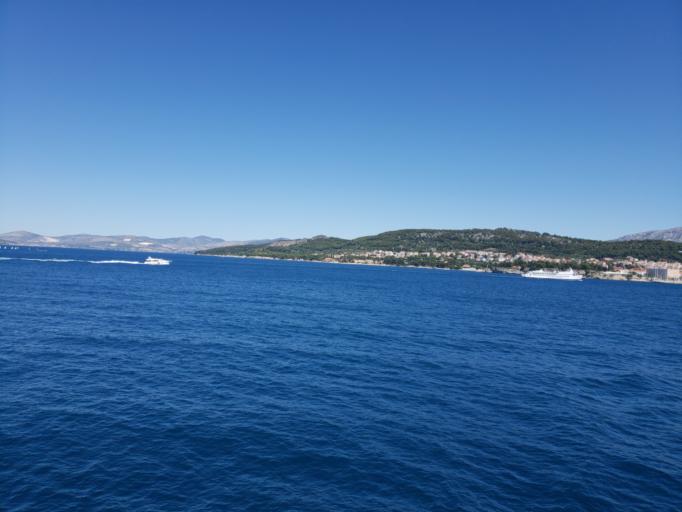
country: HR
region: Splitsko-Dalmatinska
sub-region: Grad Split
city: Split
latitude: 43.4907
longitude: 16.4328
